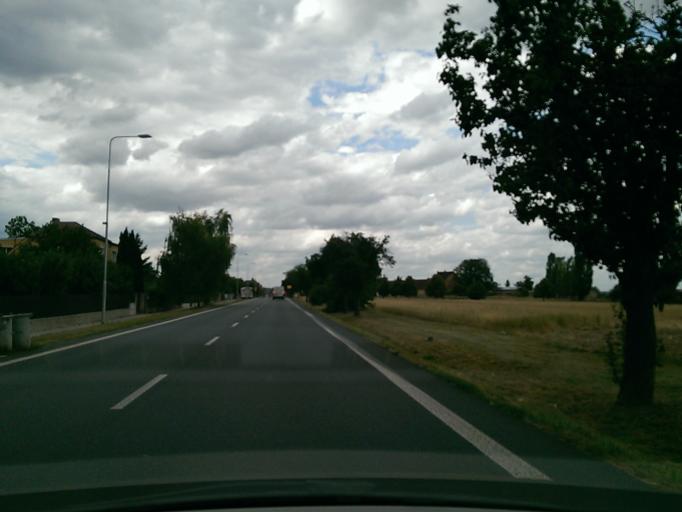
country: CZ
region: Central Bohemia
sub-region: Okres Nymburk
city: Nymburk
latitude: 50.2168
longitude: 15.0304
